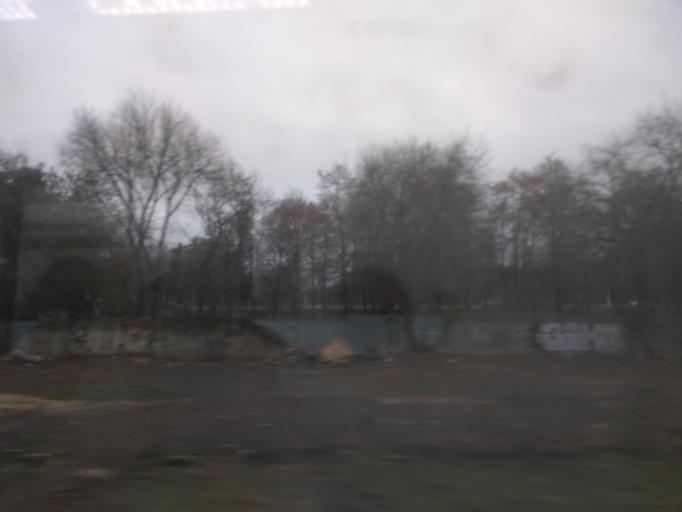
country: RU
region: Moscow
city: Tekstil'shchiki
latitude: 55.7055
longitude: 37.7296
